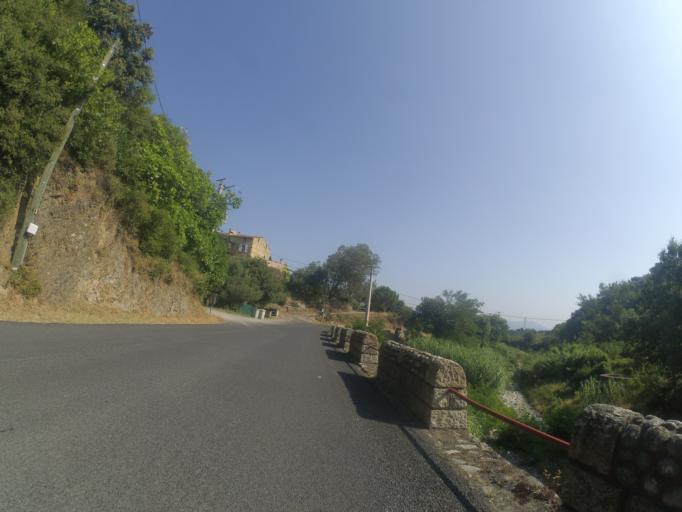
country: FR
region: Languedoc-Roussillon
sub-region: Departement des Pyrenees-Orientales
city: Ille-sur-Tet
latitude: 42.6509
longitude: 2.6225
